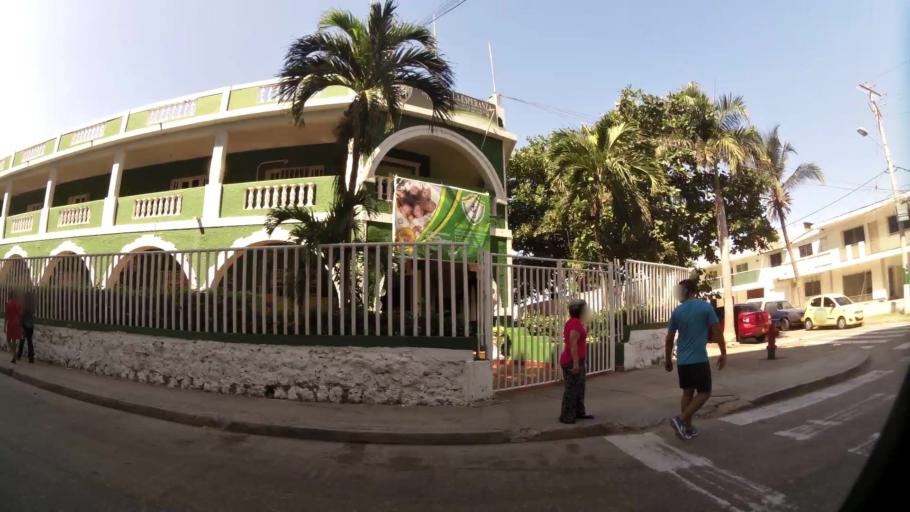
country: CO
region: Bolivar
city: Cartagena
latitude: 10.4441
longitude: -75.5235
